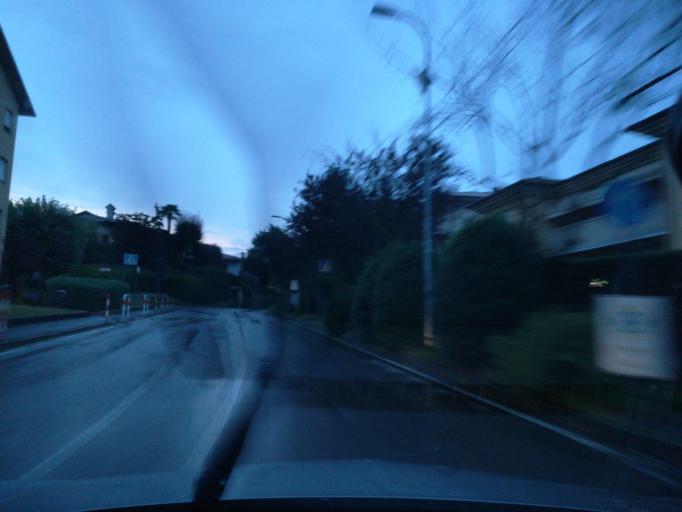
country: IT
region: Lombardy
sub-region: Provincia di Bergamo
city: Almenno San Bartolomeo
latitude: 45.7415
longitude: 9.5810
